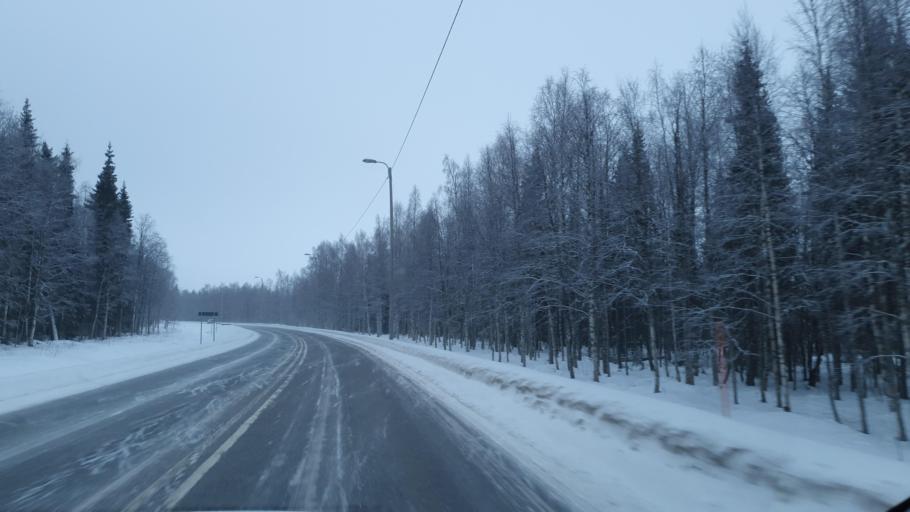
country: FI
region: Lapland
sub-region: Torniolaakso
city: Ylitornio
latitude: 66.2526
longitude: 23.7143
